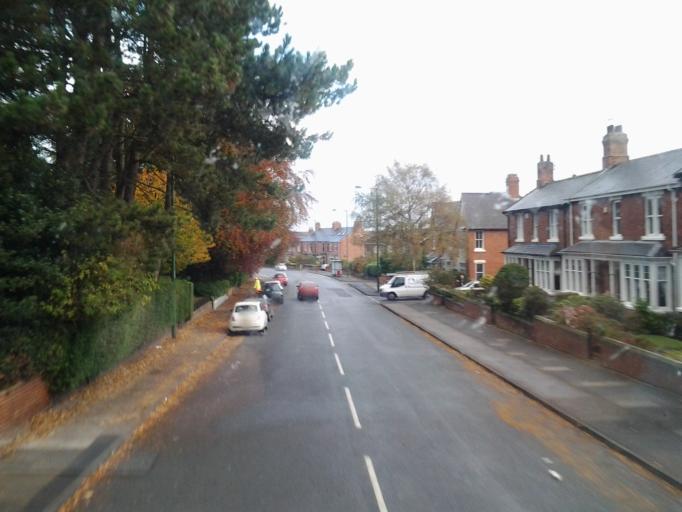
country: GB
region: England
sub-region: County Durham
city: Chester-le-Street
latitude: 54.8481
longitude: -1.5736
